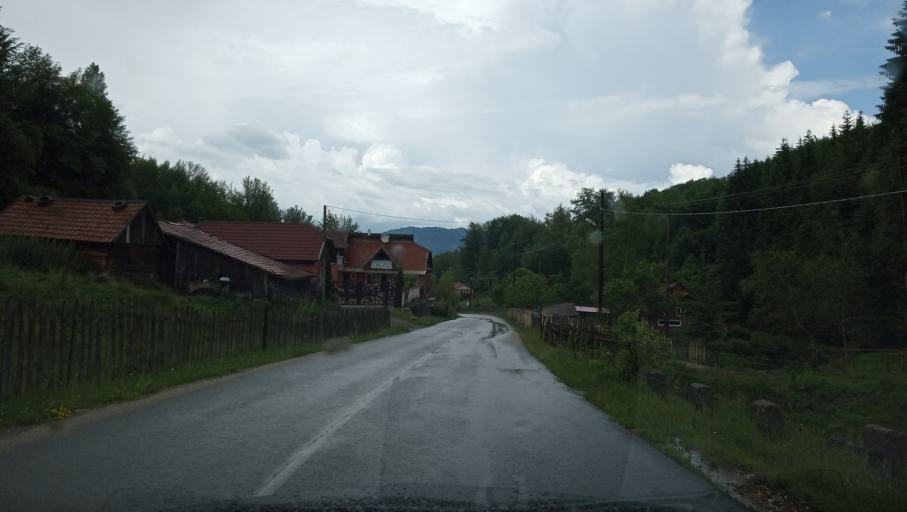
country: RO
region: Hunedoara
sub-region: Oras Petrila
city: Petrila
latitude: 45.4023
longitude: 23.4144
